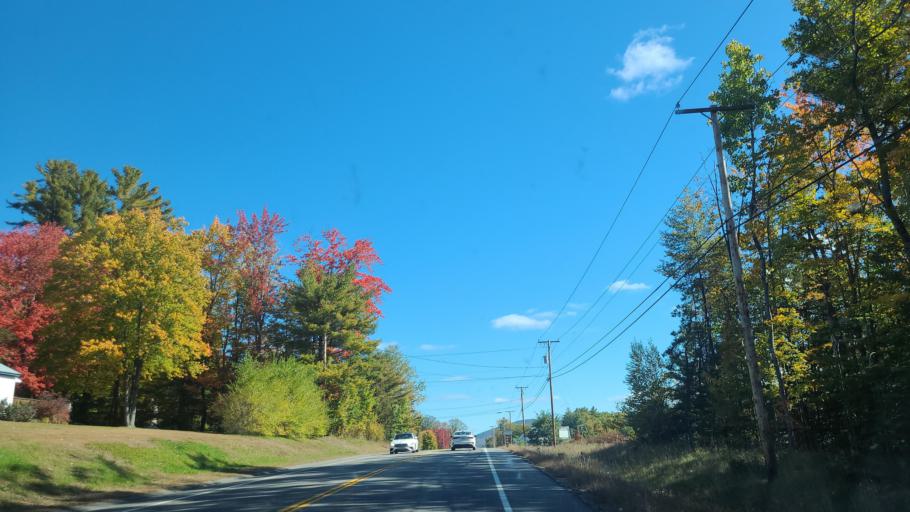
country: US
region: Maine
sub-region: Oxford County
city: Fryeburg
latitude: 44.0229
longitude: -70.9469
